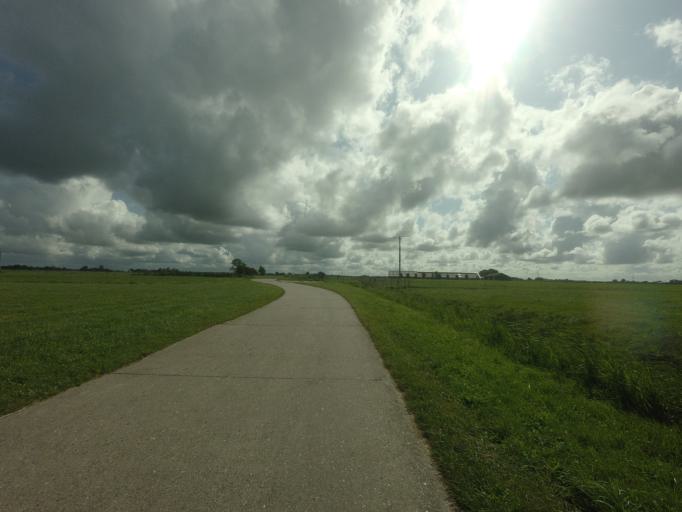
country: NL
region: Friesland
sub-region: Sudwest Fryslan
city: Scharnegoutum
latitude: 53.0746
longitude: 5.6369
